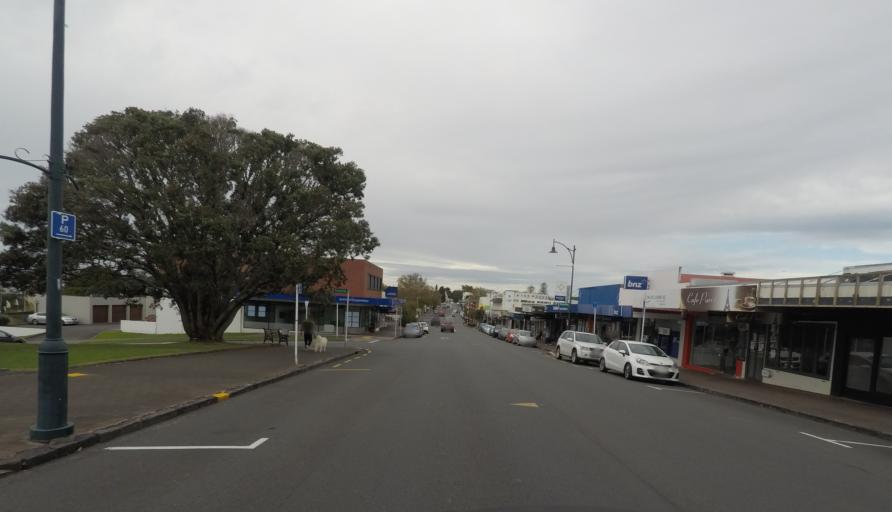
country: NZ
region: Auckland
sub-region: Auckland
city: Pakuranga
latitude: -36.8933
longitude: 174.9307
